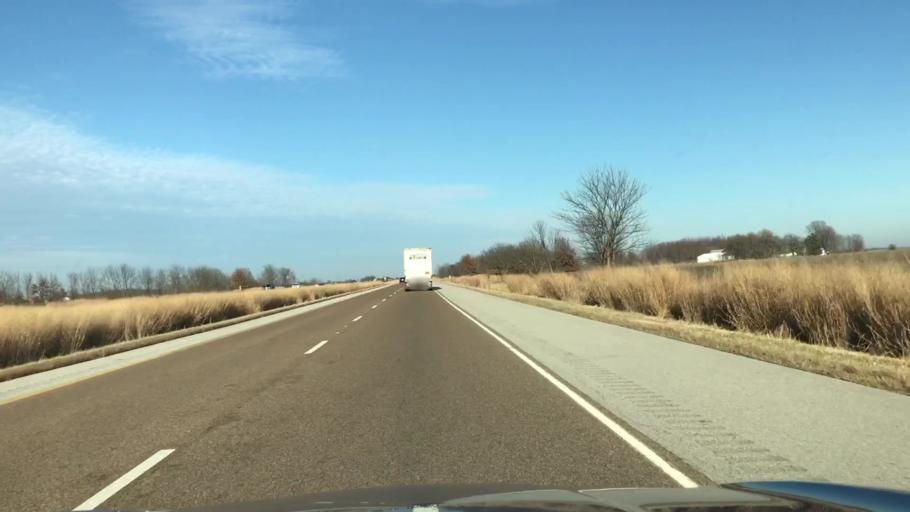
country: US
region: Illinois
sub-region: Macoupin County
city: Mount Olive
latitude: 39.1287
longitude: -89.7125
